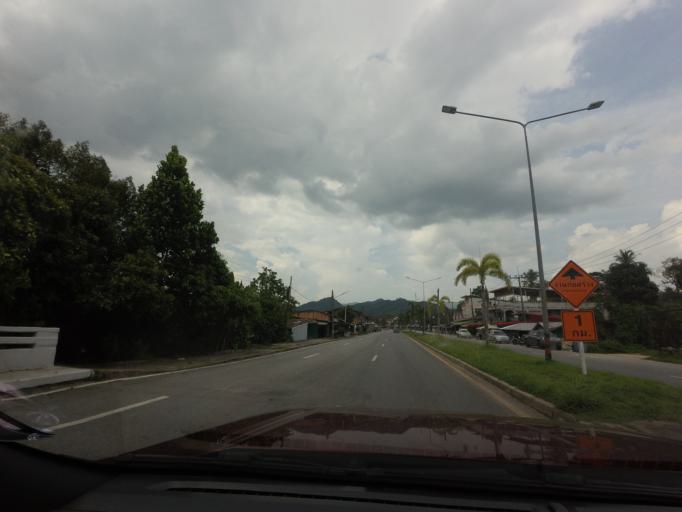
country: TH
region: Yala
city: Ban Nang Sata
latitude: 6.2947
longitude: 101.2994
